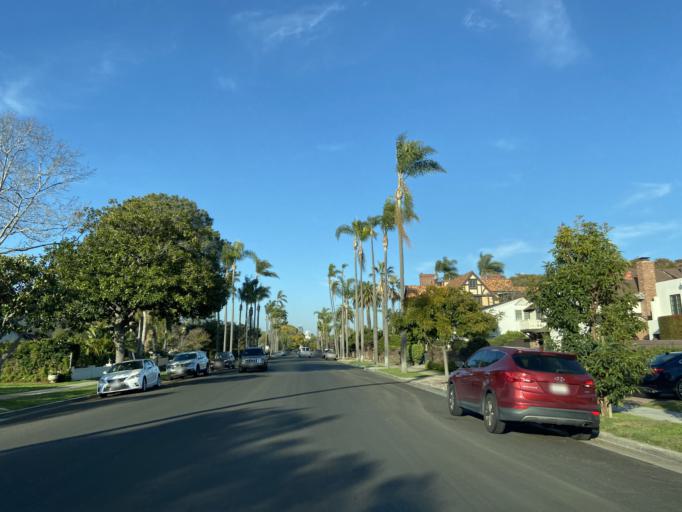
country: US
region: California
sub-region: San Diego County
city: Coronado
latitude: 32.6877
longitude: -117.1745
